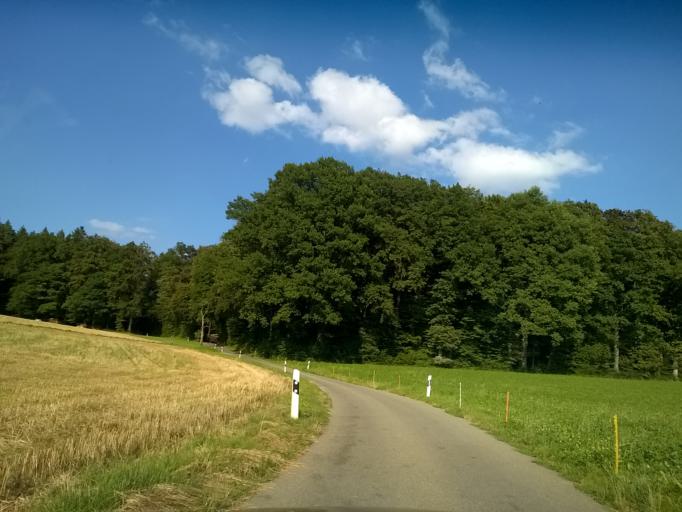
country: CH
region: Zurich
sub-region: Bezirk Buelach
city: Embrach / Embrach (Dorfkern)
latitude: 47.4948
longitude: 8.6210
